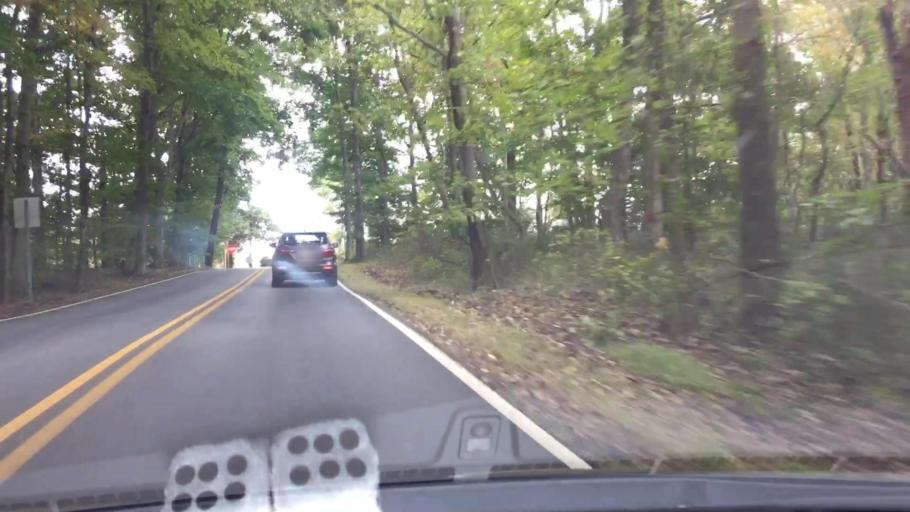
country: US
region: Pennsylvania
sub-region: Delaware County
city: Lima
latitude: 39.9301
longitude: -75.4276
